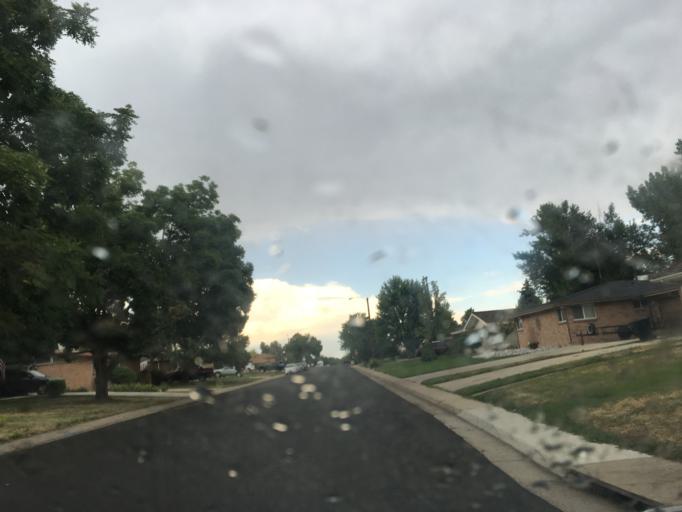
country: US
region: Colorado
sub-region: Arapahoe County
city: Sheridan
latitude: 39.6775
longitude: -105.0490
